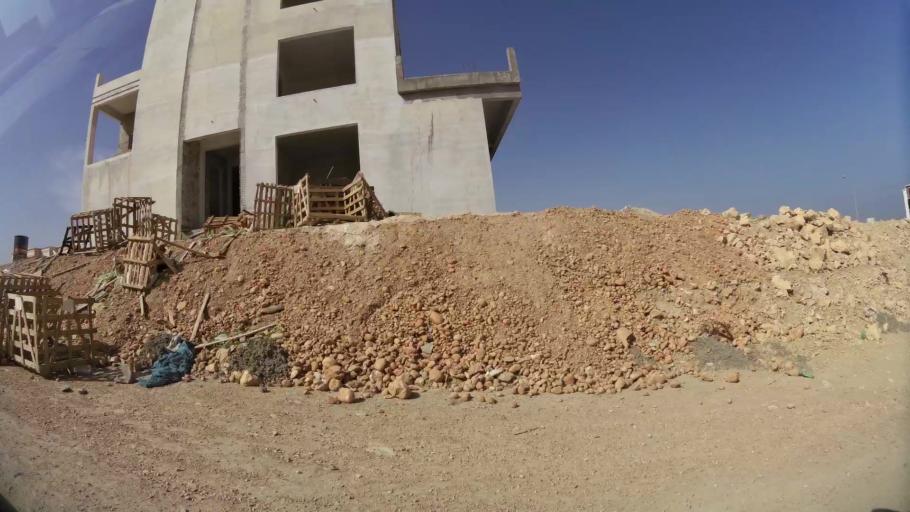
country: OM
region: Zufar
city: Salalah
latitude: 16.9994
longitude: 54.0162
